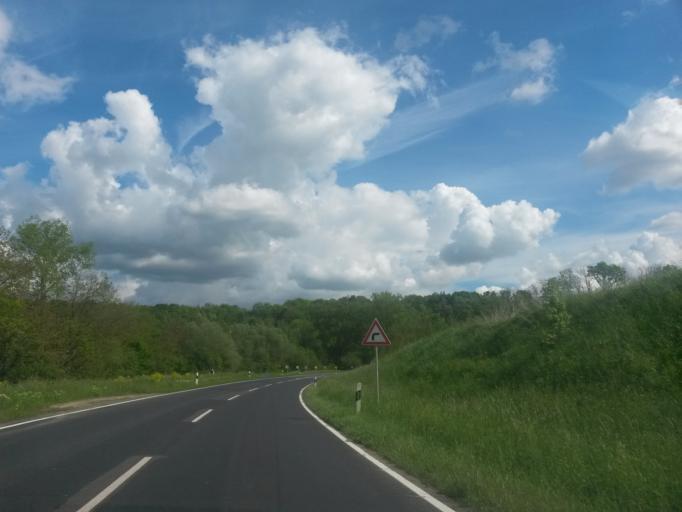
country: DE
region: Bavaria
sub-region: Regierungsbezirk Unterfranken
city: Rimpar
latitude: 49.8472
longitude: 9.9588
